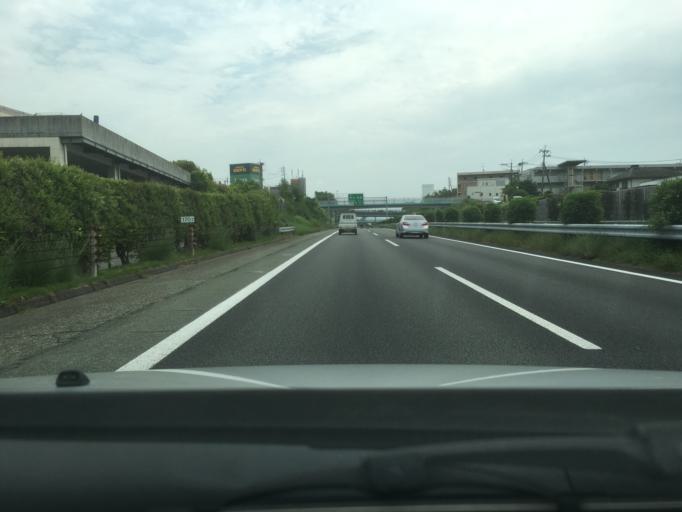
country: JP
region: Kumamoto
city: Kumamoto
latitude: 32.8390
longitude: 130.7764
